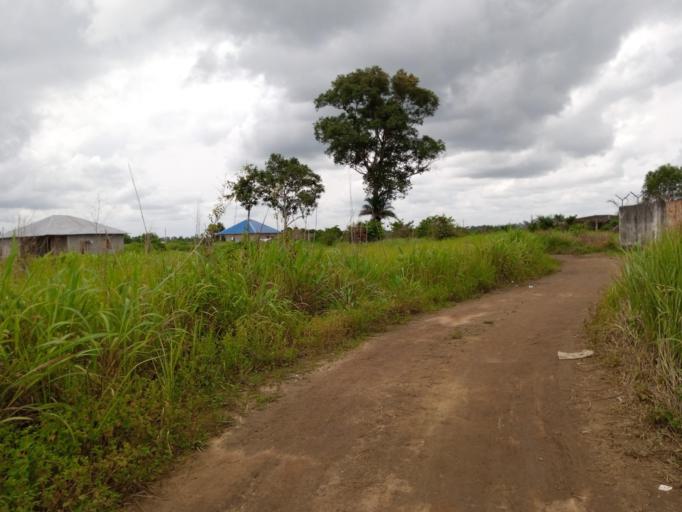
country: SL
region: Southern Province
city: Moyamba
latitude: 8.1696
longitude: -12.4182
